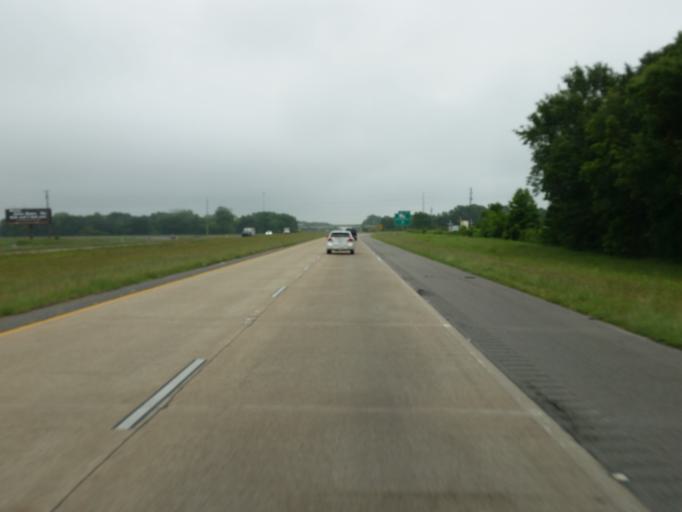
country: US
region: Louisiana
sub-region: Madison Parish
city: Tallulah
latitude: 32.3827
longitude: -91.1792
